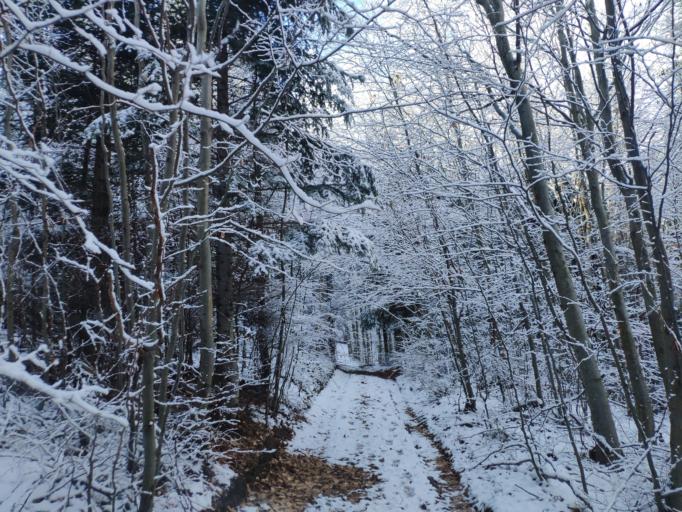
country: SK
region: Kosicky
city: Moldava nad Bodvou
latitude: 48.7436
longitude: 21.0908
